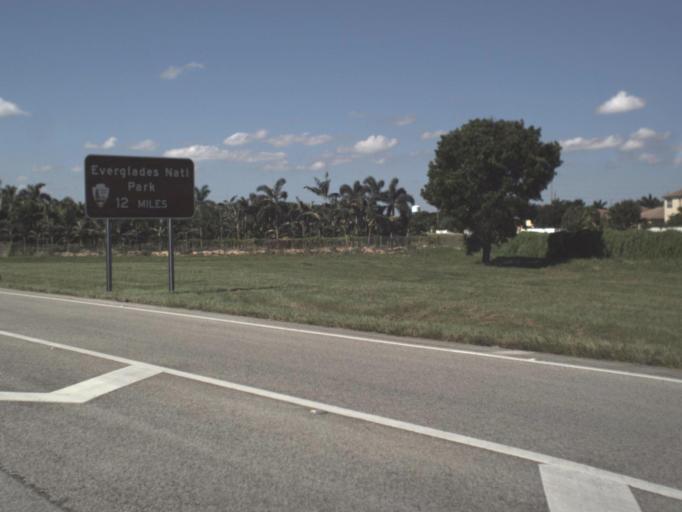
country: US
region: Florida
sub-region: Miami-Dade County
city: Leisure City
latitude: 25.4728
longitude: -80.4476
